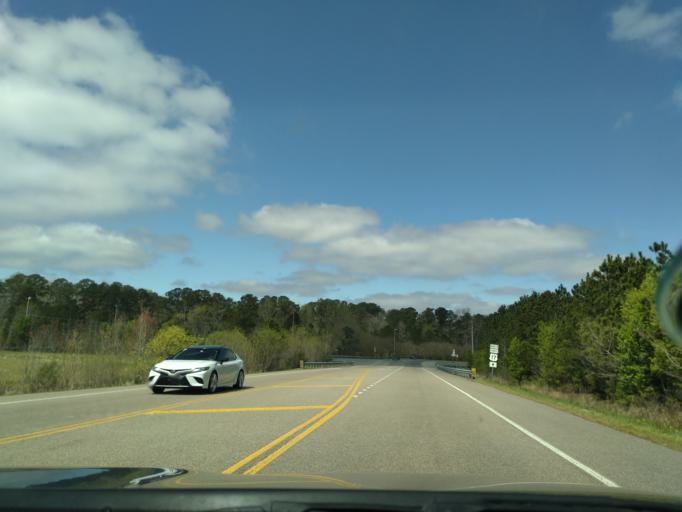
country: US
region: Virginia
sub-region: City of Portsmouth
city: Portsmouth Heights
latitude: 36.6914
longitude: -76.3555
